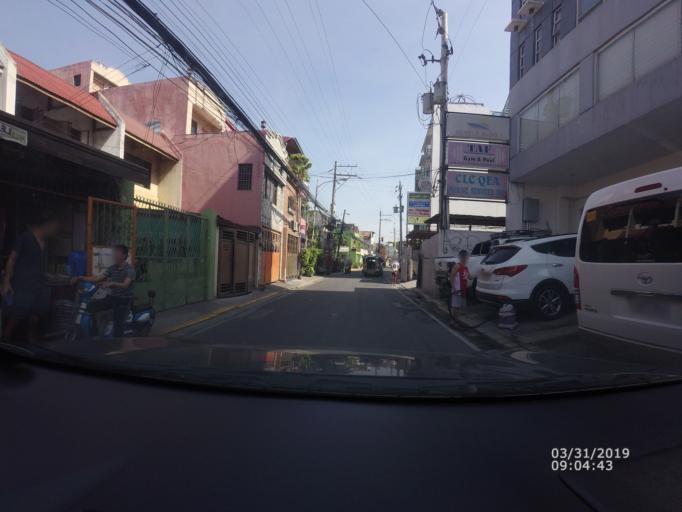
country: PH
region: Metro Manila
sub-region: Mandaluyong
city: Mandaluyong City
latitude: 14.5819
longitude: 121.0209
